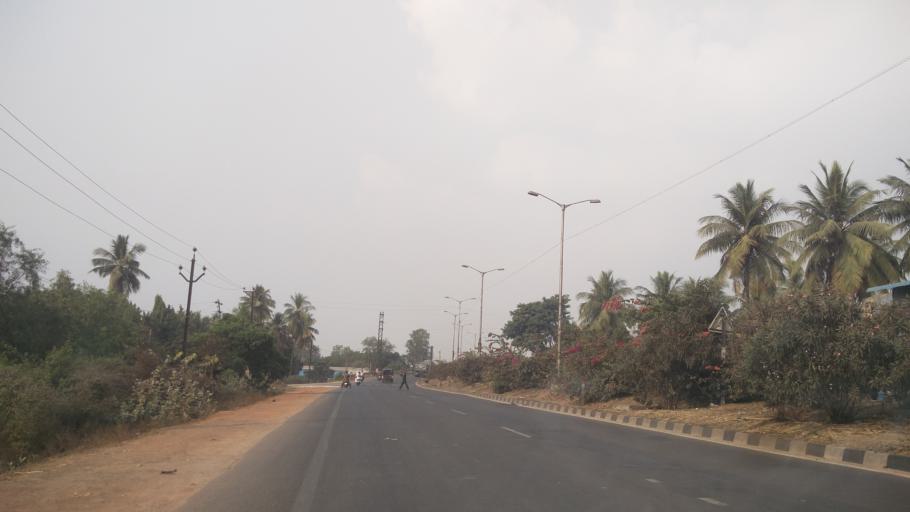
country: IN
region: Andhra Pradesh
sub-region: East Godavari
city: Rajahmundry
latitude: 16.9547
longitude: 81.7927
